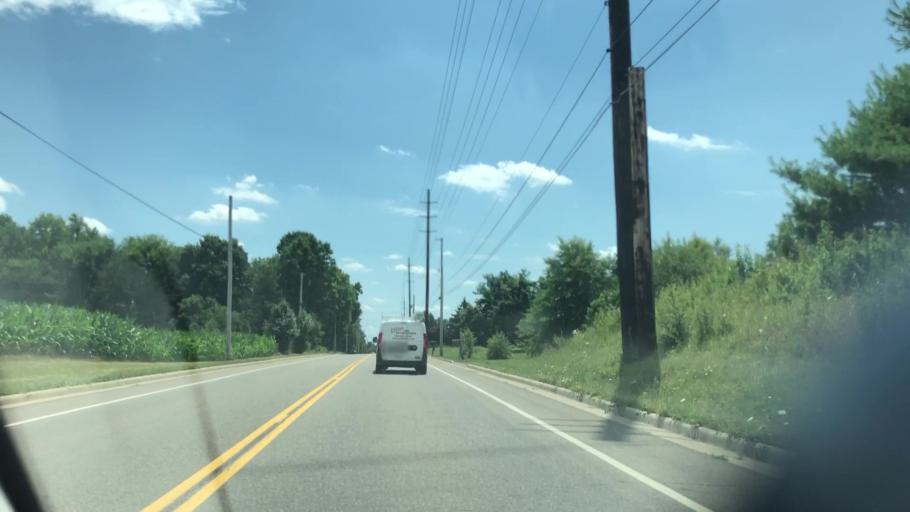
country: US
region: Ohio
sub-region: Summit County
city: Greensburg
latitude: 40.8763
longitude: -81.4997
